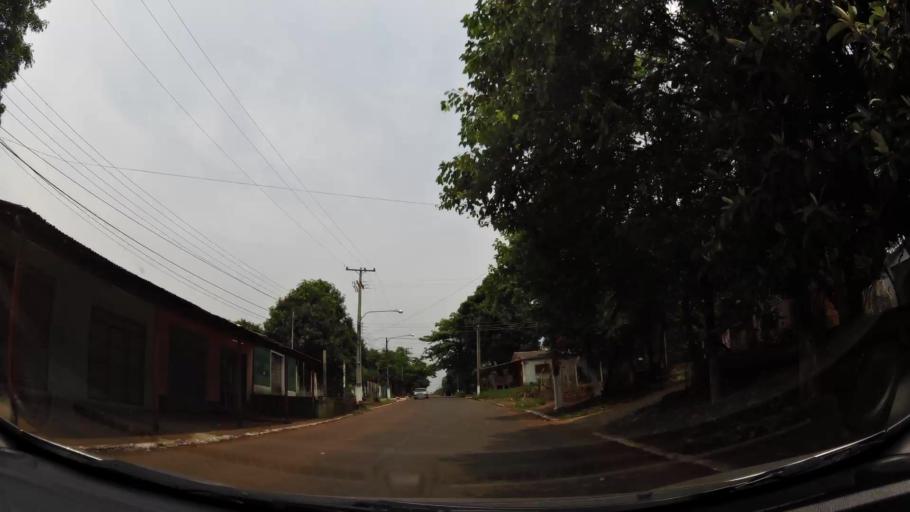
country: BR
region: Parana
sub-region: Foz Do Iguacu
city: Foz do Iguacu
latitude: -25.5719
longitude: -54.6053
